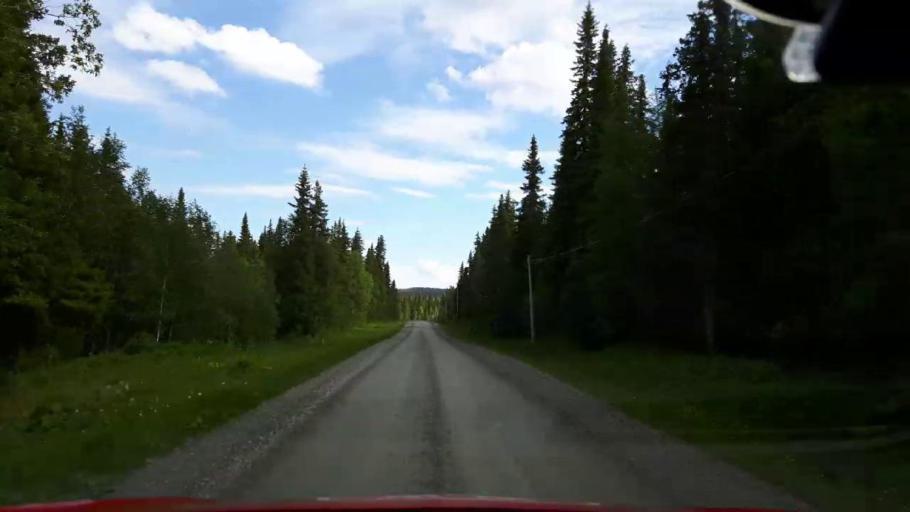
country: SE
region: Jaemtland
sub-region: Krokoms Kommun
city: Valla
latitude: 63.8173
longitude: 14.0456
